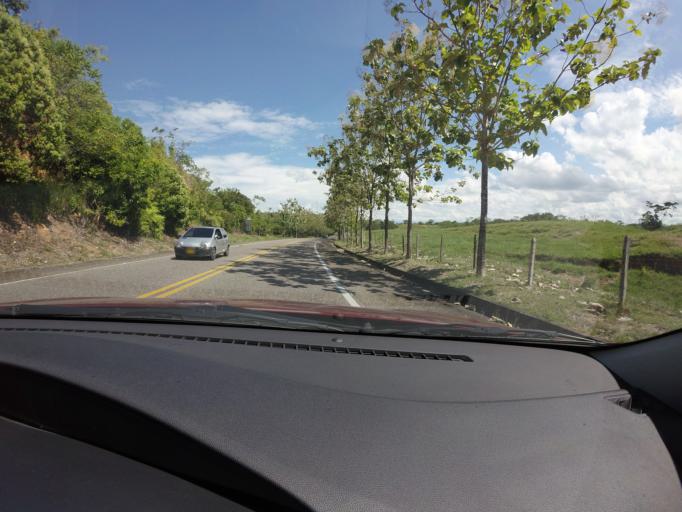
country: CO
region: Antioquia
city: Puerto Triunfo
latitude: 5.9001
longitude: -74.6303
